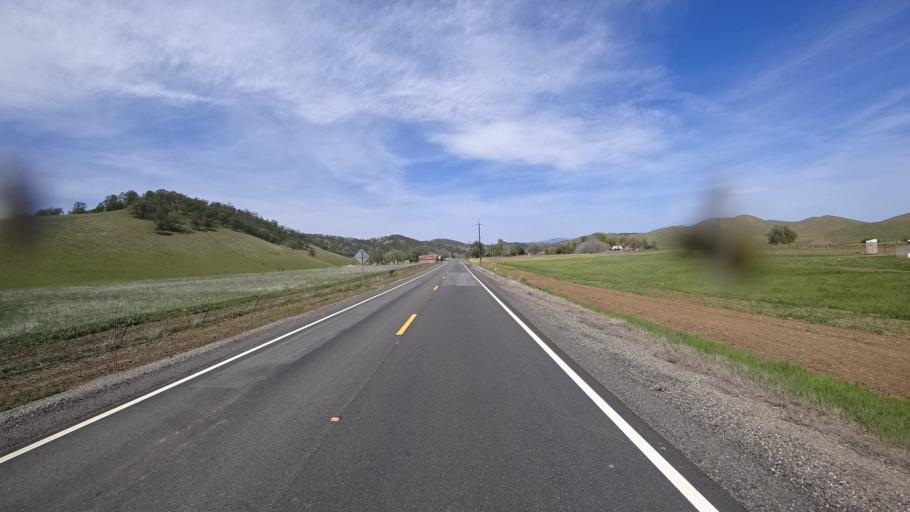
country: US
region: California
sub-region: Glenn County
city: Willows
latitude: 39.5874
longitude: -122.4480
